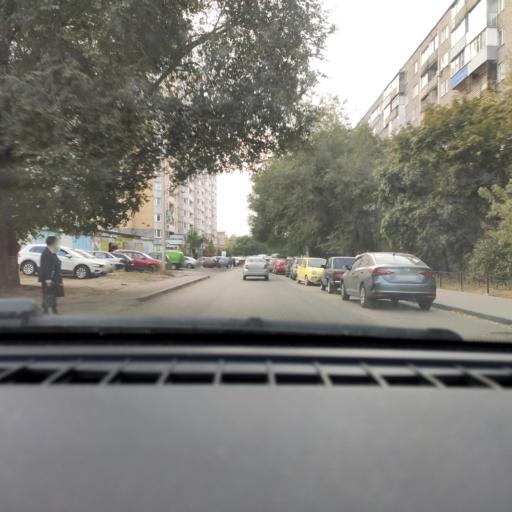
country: RU
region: Voronezj
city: Voronezh
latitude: 51.6470
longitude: 39.2373
